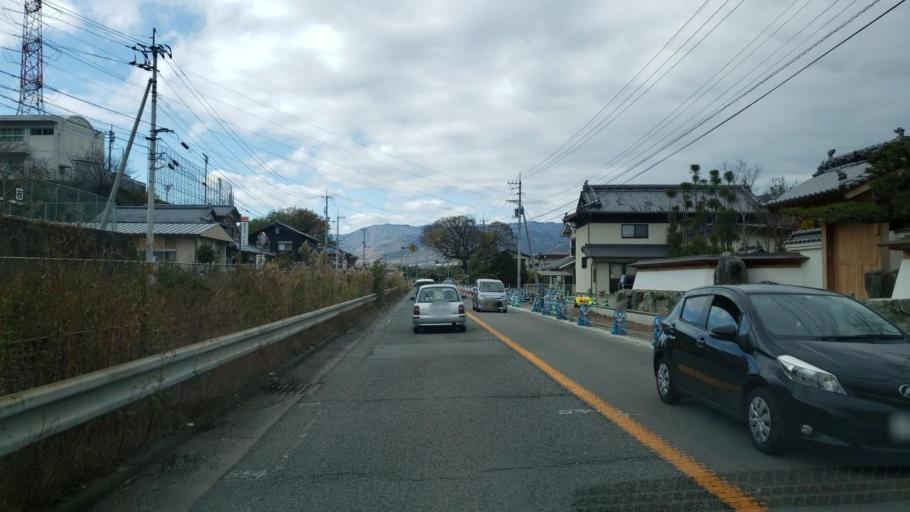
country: JP
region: Tokushima
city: Wakimachi
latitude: 34.0558
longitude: 134.1294
